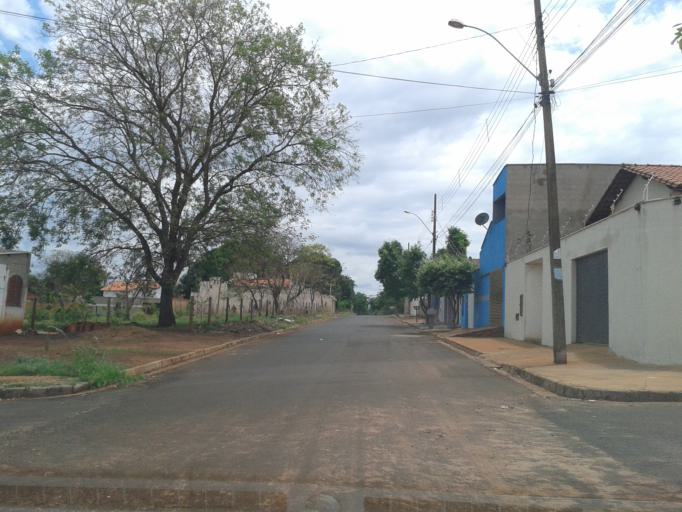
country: BR
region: Minas Gerais
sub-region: Ituiutaba
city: Ituiutaba
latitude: -18.9951
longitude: -49.4613
